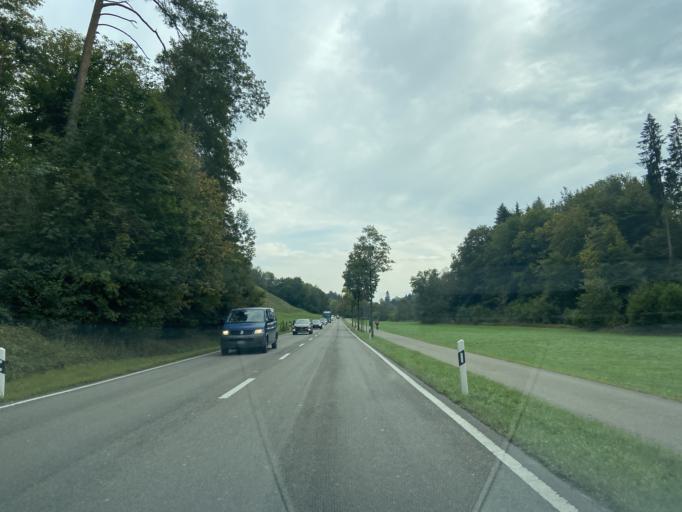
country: CH
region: Zurich
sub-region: Bezirk Pfaeffikon
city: Effretikon / Watt
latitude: 47.4238
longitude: 8.7127
